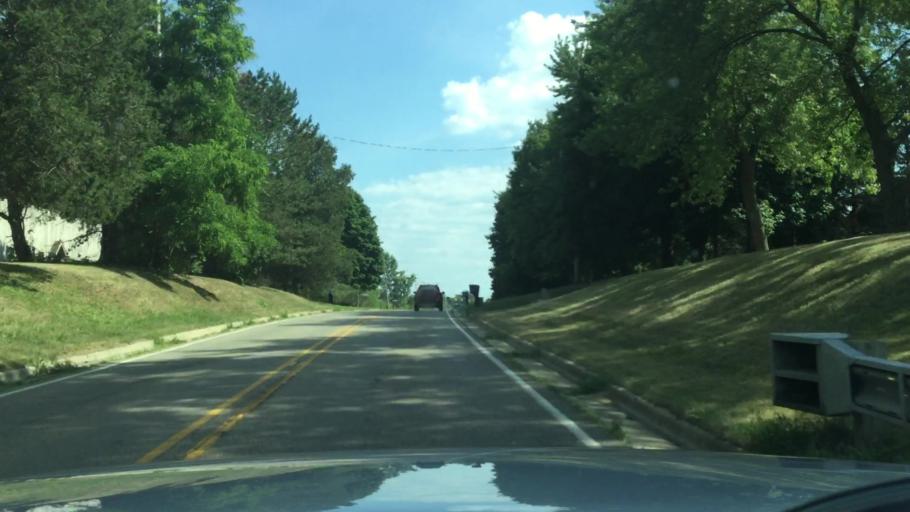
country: US
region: Michigan
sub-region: Genesee County
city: Grand Blanc
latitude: 42.9355
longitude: -83.5973
